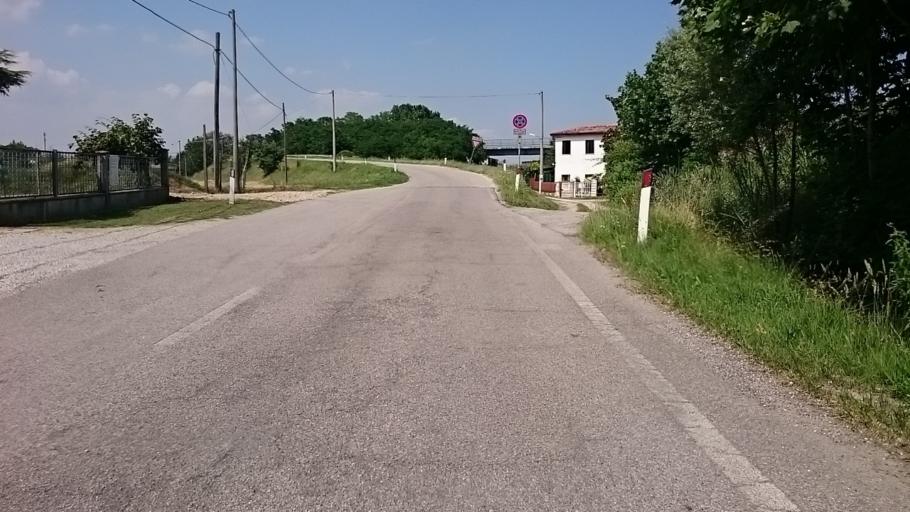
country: IT
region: Veneto
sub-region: Provincia di Padova
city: Mandriola-Sant'Agostino
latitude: 45.3553
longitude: 11.8540
